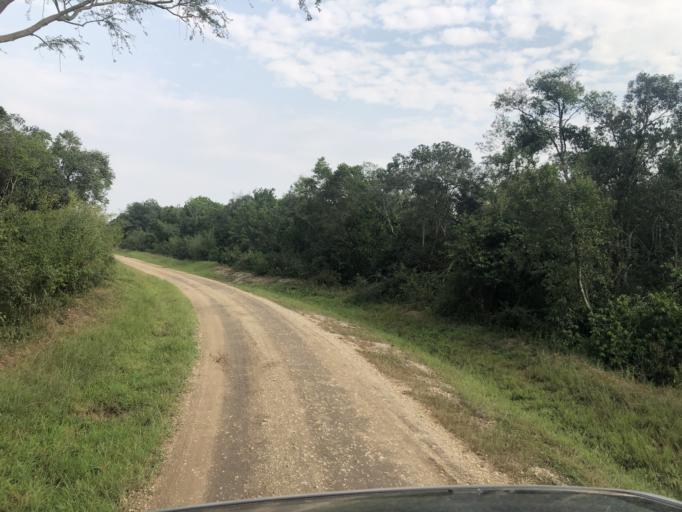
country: UG
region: Western Region
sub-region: Rubirizi District
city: Rubirizi
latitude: -0.4296
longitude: 29.7877
